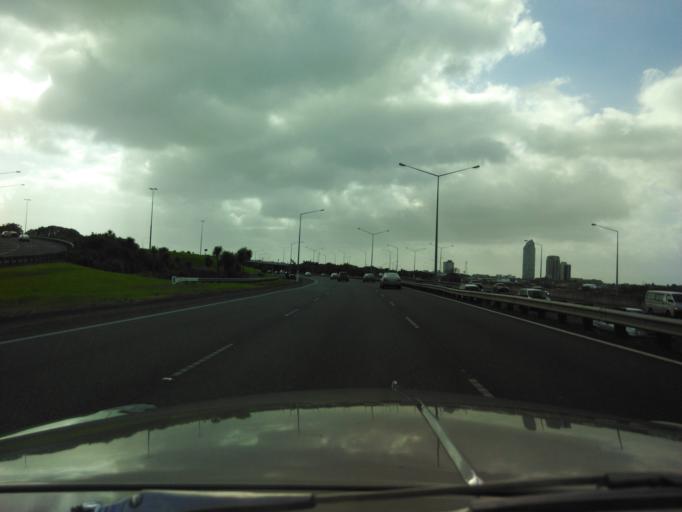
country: NZ
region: Auckland
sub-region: Auckland
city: North Shore
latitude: -36.8025
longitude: 174.7609
